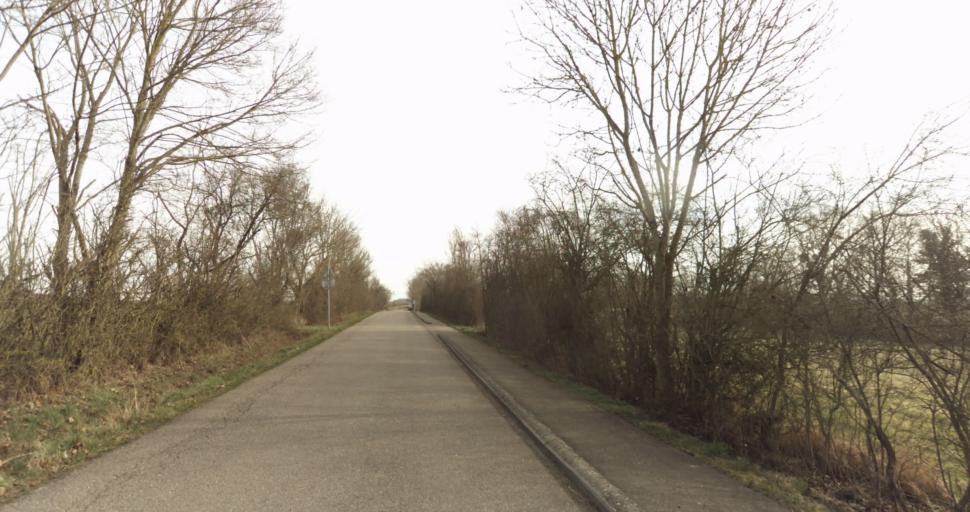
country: FR
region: Lorraine
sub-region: Departement de Meurthe-et-Moselle
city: Jarny
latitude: 49.1508
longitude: 5.8996
